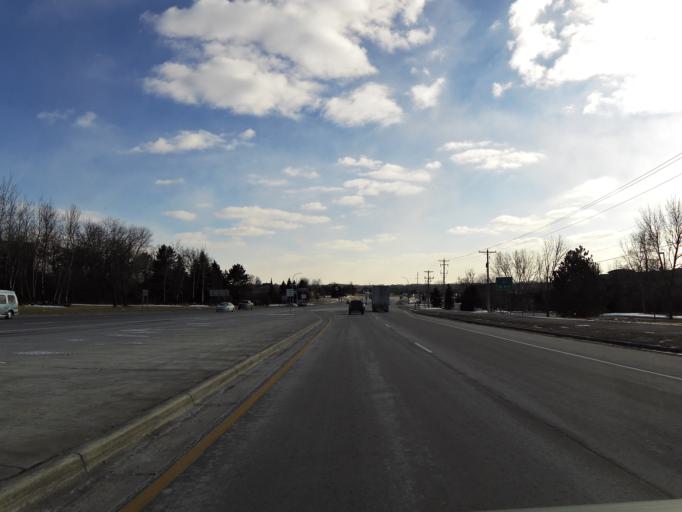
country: US
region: Minnesota
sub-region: Dakota County
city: Mendota Heights
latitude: 44.8572
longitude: -93.1286
